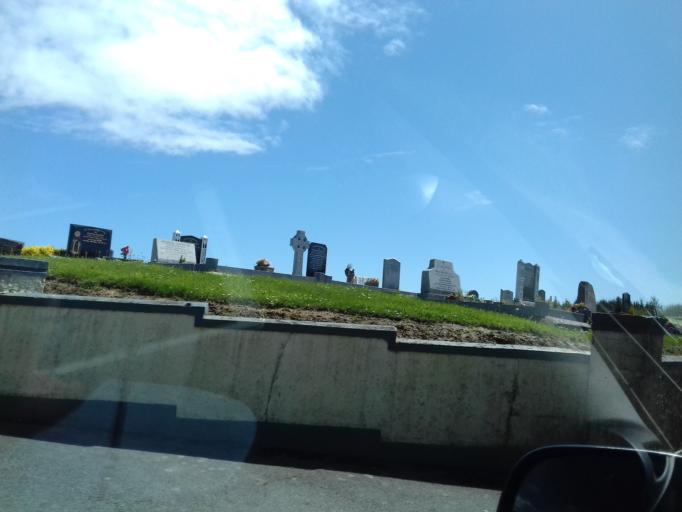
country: IE
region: Munster
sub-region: Waterford
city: Dunmore East
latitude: 52.2050
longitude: -6.8559
